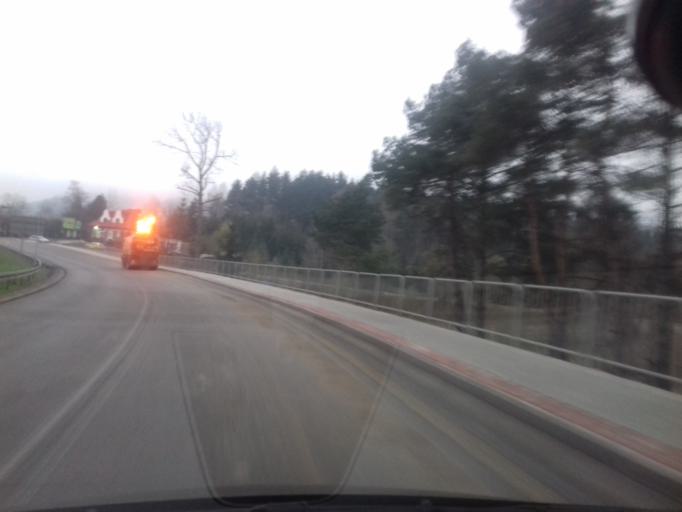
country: PL
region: Lesser Poland Voivodeship
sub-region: Powiat limanowski
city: Kasina Wielka
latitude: 49.7046
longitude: 20.1347
